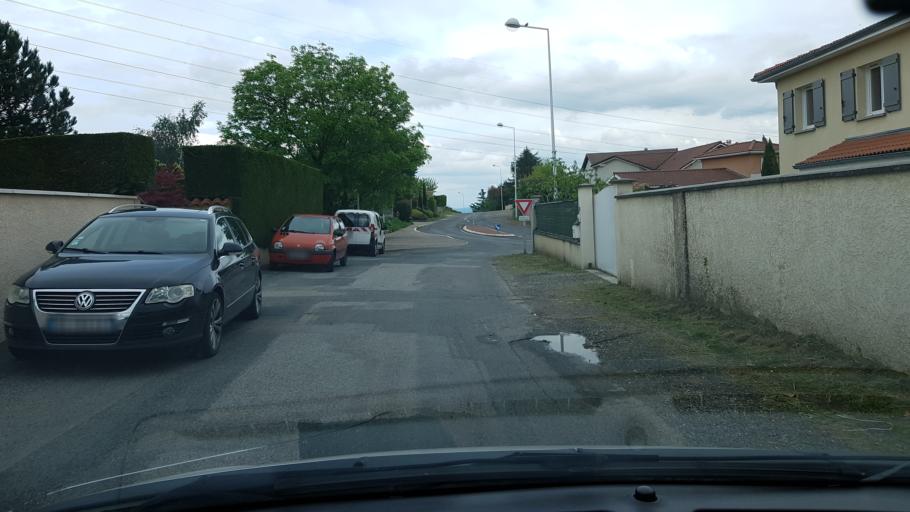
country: FR
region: Rhone-Alpes
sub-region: Departement du Rhone
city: Orlienas
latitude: 45.6453
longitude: 4.6915
